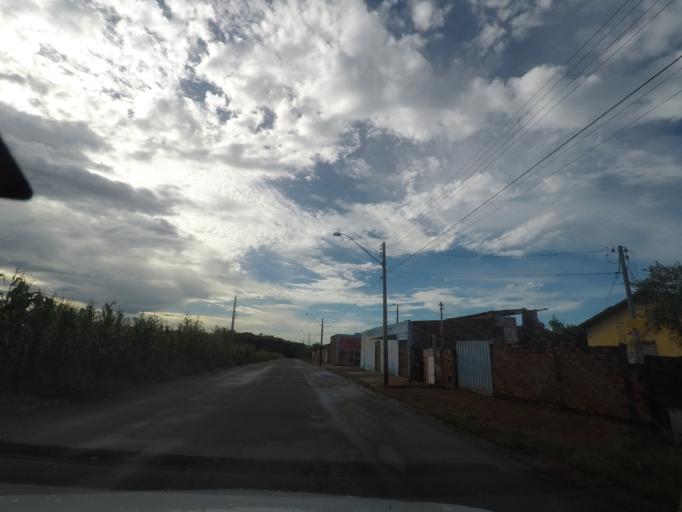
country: BR
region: Goias
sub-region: Aparecida De Goiania
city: Aparecida de Goiania
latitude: -16.7788
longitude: -49.3842
